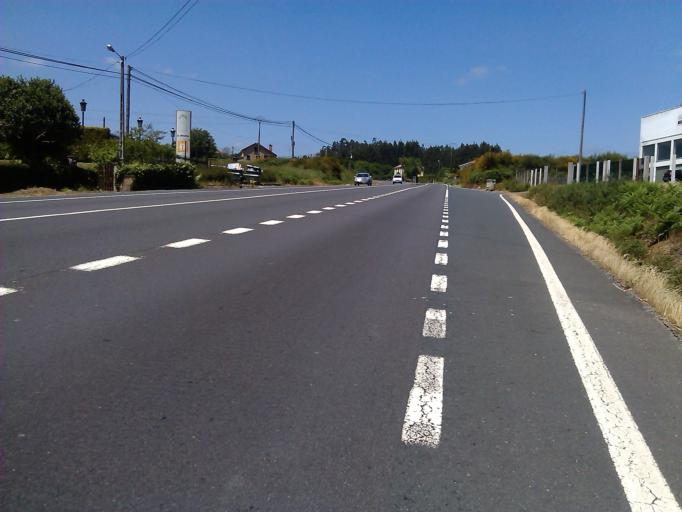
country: ES
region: Galicia
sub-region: Provincia da Coruna
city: Oroso
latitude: 42.9079
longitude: -8.3969
